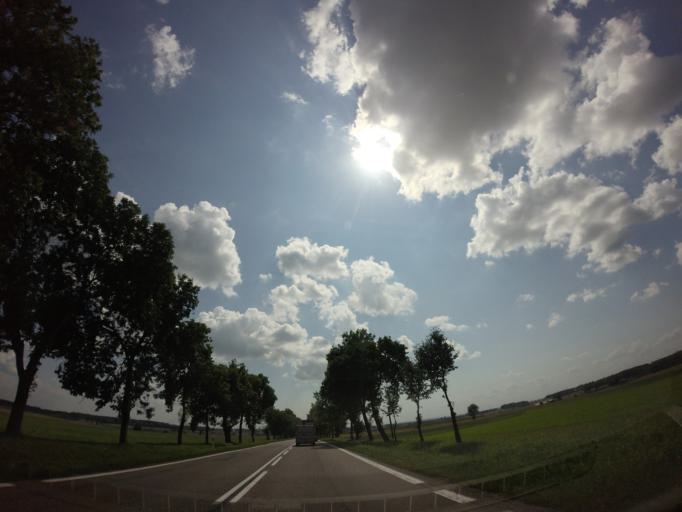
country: PL
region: Podlasie
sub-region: Powiat lomzynski
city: Piatnica
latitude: 53.2665
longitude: 22.1288
